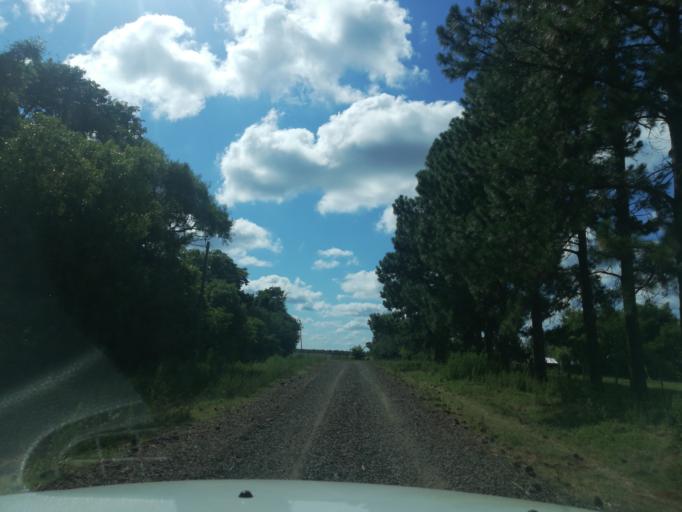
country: AR
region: Corrientes
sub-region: Departamento de San Miguel
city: San Miguel
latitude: -27.9848
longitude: -57.5752
